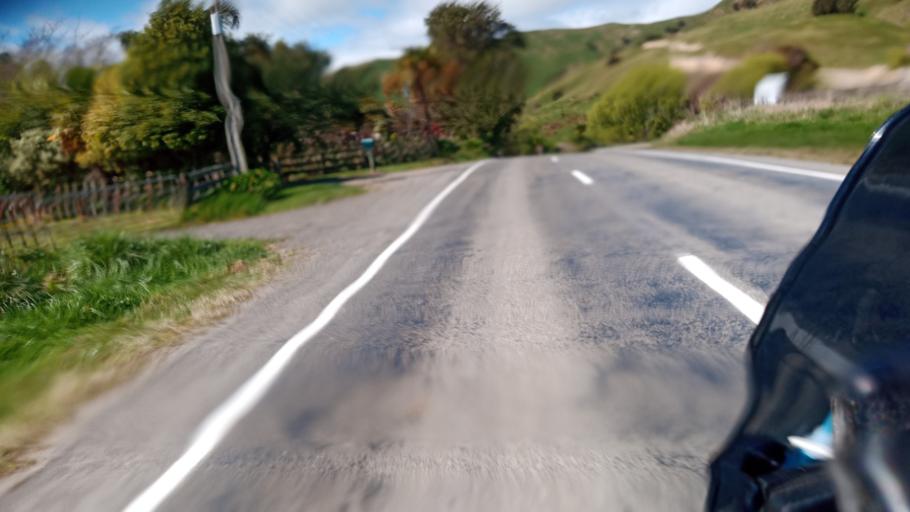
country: NZ
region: Gisborne
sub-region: Gisborne District
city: Gisborne
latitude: -38.7220
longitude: 177.8288
